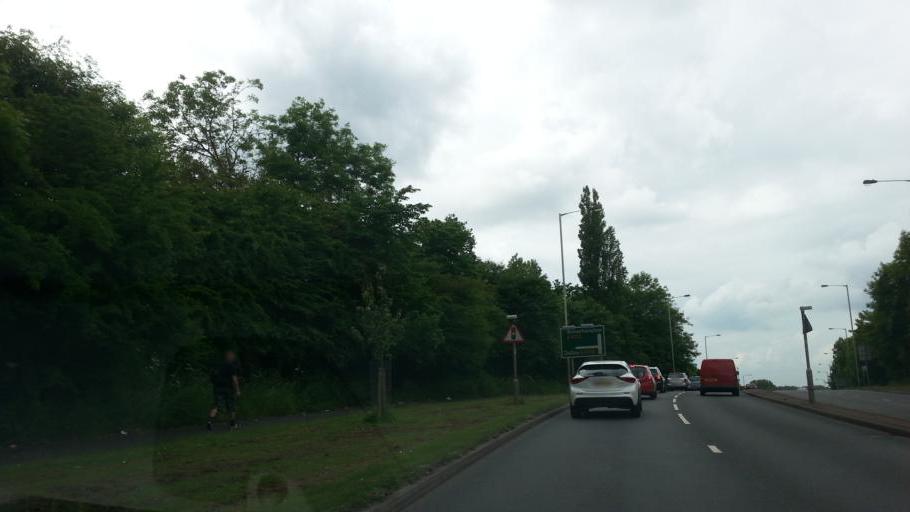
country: GB
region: England
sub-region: Sandwell
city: Tipton
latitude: 52.5256
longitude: -2.0841
